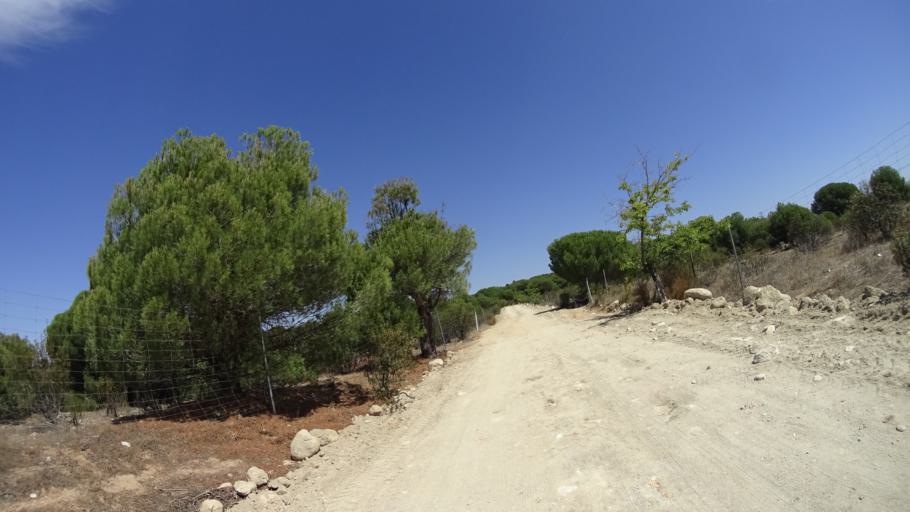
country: ES
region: Madrid
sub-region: Provincia de Madrid
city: Torrelodones
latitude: 40.5589
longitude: -3.9376
